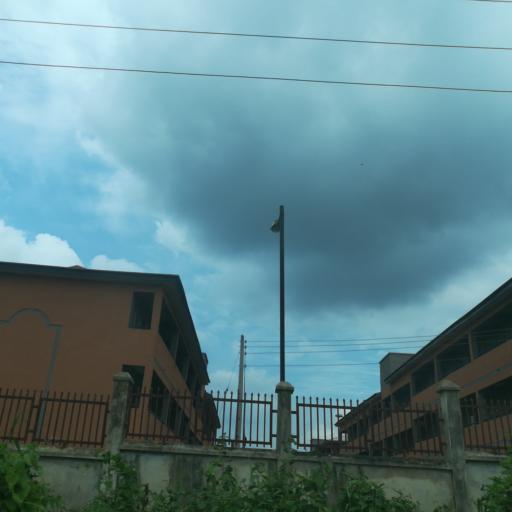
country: NG
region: Ogun
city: Odogbolu
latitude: 6.6739
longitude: 3.7116
